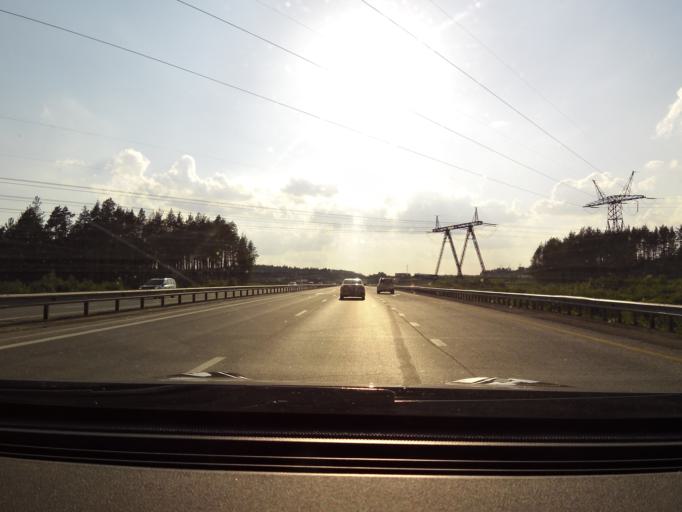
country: RU
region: Sverdlovsk
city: Severka
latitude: 56.8329
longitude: 60.3291
